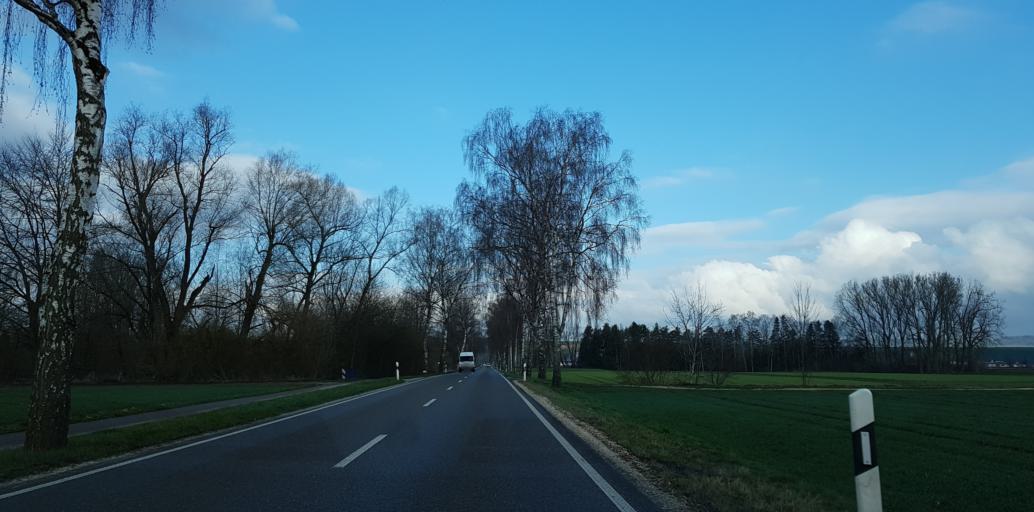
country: DE
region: Baden-Wuerttemberg
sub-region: Tuebingen Region
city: Erbach
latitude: 48.3289
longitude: 9.9245
